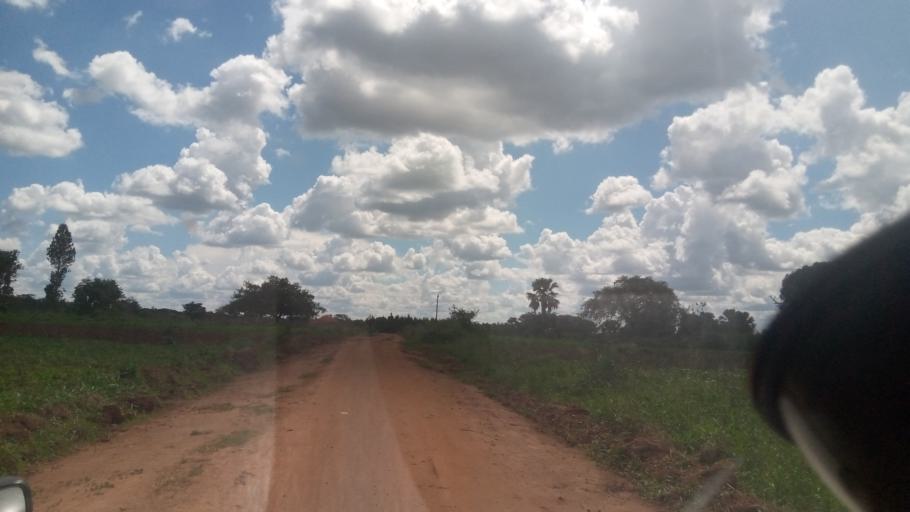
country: UG
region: Northern Region
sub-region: Lira District
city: Lira
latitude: 2.2318
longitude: 32.9055
